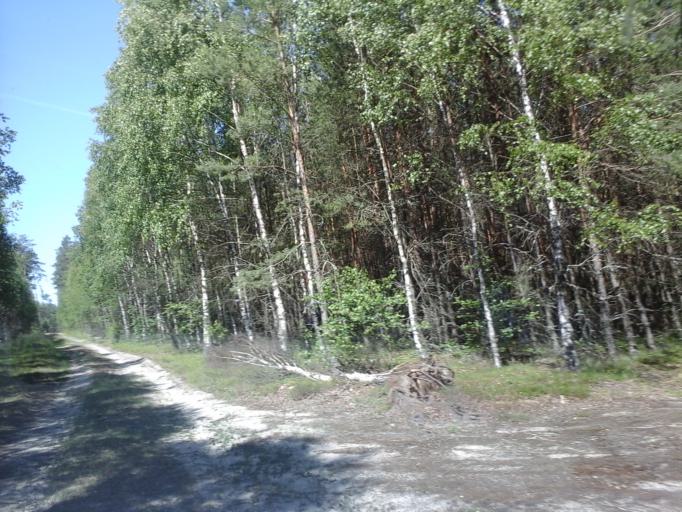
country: PL
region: West Pomeranian Voivodeship
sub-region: Powiat walecki
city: Tuczno
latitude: 53.2115
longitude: 16.0191
